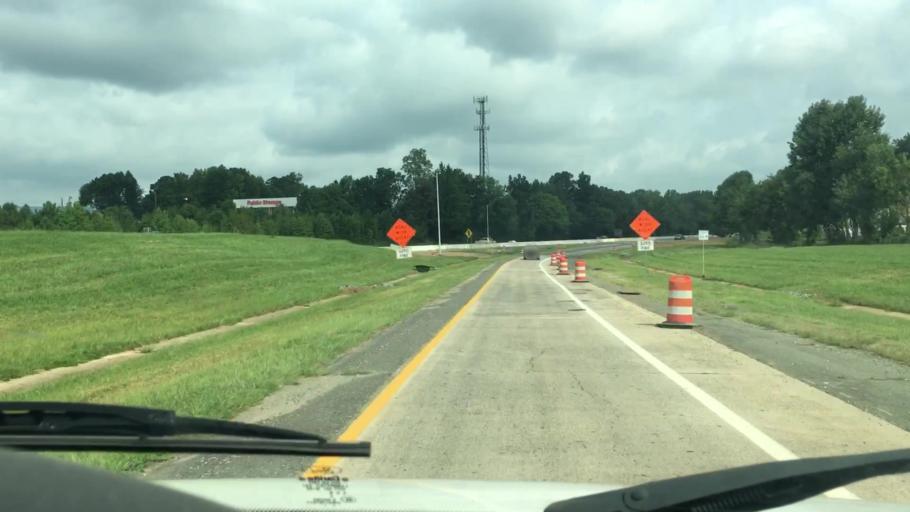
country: US
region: North Carolina
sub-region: Mecklenburg County
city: Charlotte
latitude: 35.3091
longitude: -80.8466
